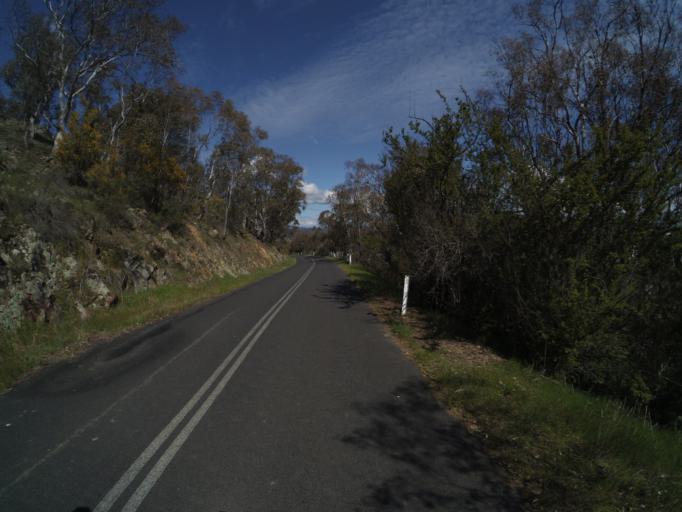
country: AU
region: New South Wales
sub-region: Yass Valley
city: Yass
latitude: -34.9892
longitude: 148.8411
